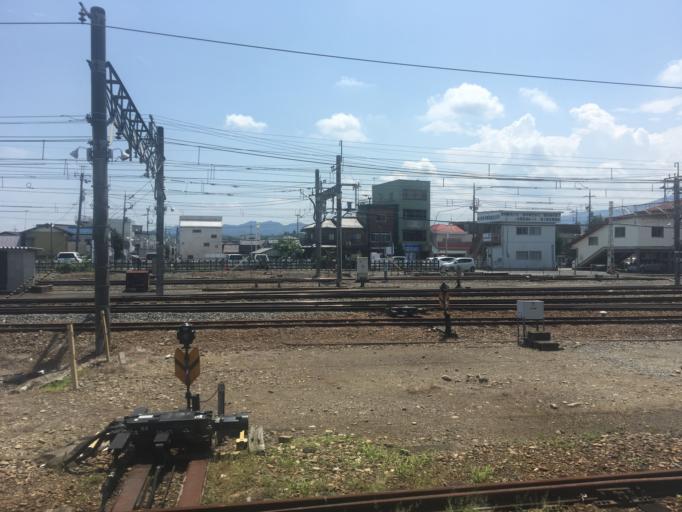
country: JP
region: Saitama
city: Yorii
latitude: 36.1181
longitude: 139.1952
